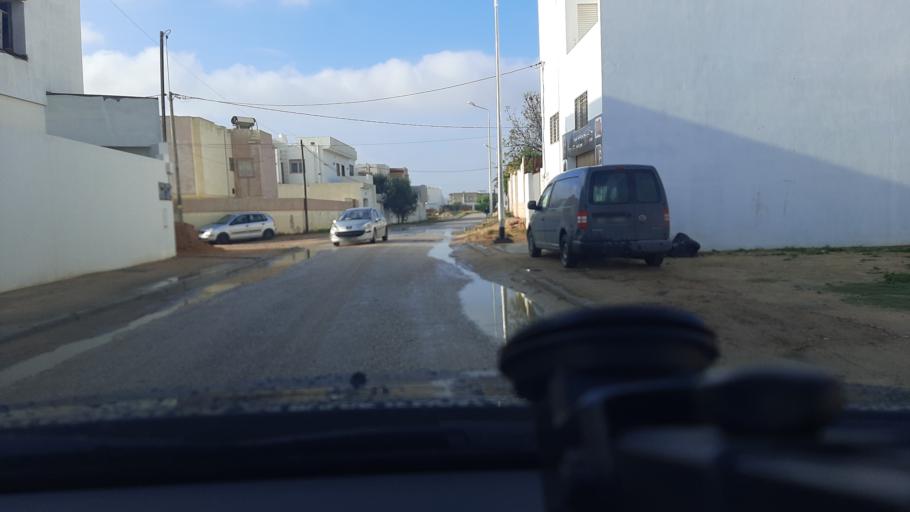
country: TN
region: Safaqis
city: Sfax
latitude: 34.7423
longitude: 10.7151
